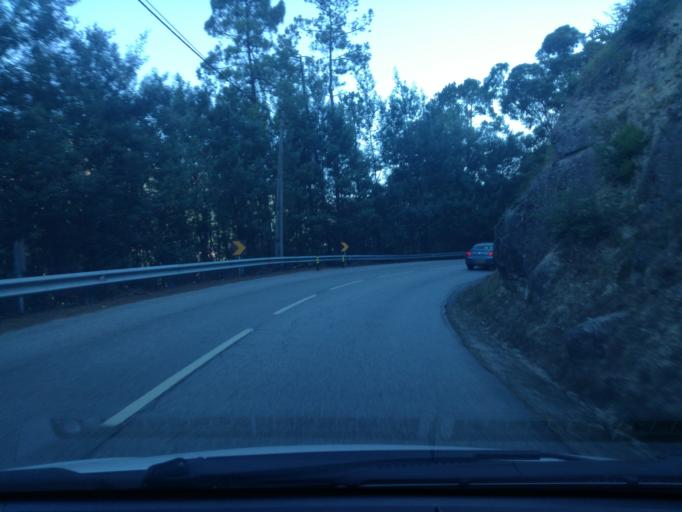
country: PT
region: Braga
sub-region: Vieira do Minho
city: Real
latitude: 41.6926
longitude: -8.1721
